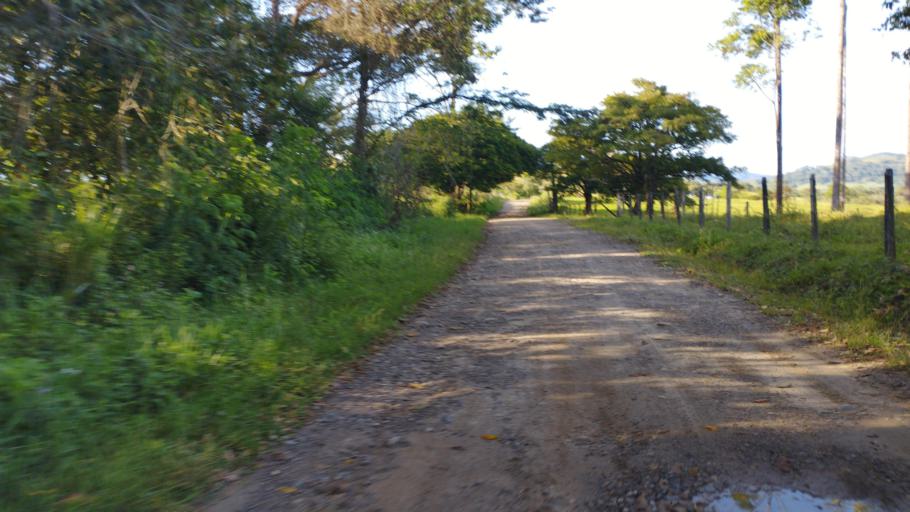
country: CO
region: Casanare
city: Sabanalarga
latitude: 4.7995
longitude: -73.0920
